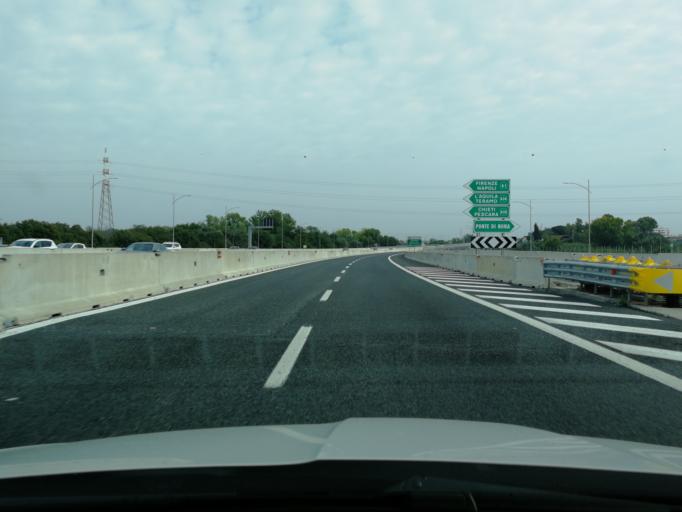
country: IT
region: Latium
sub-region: Citta metropolitana di Roma Capitale
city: Setteville
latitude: 41.9234
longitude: 12.6468
